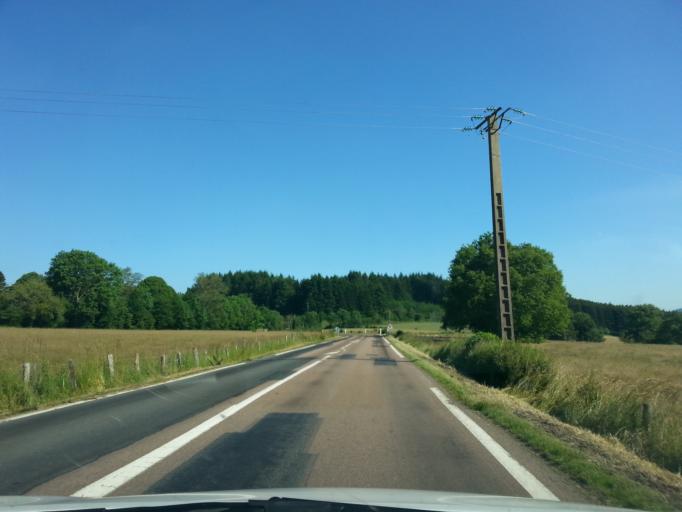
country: FR
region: Rhone-Alpes
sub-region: Departement du Rhone
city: Beaujeu
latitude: 46.1649
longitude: 4.4730
